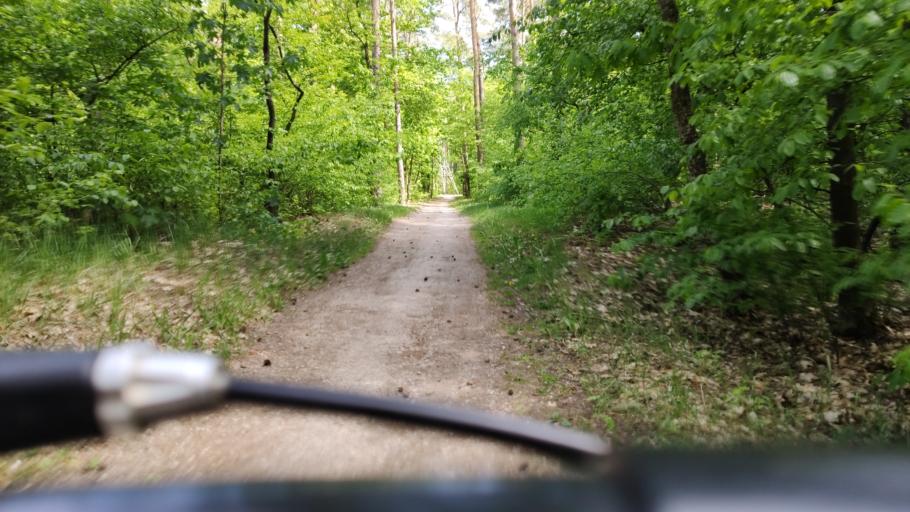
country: PL
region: Kujawsko-Pomorskie
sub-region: Wloclawek
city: Wloclawek
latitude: 52.6375
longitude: 19.1077
